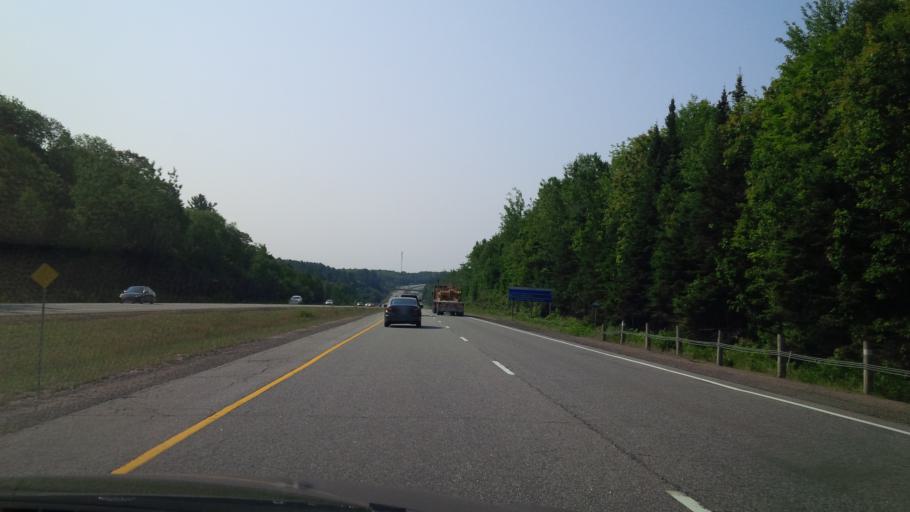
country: CA
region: Ontario
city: Bracebridge
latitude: 45.0965
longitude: -79.3052
